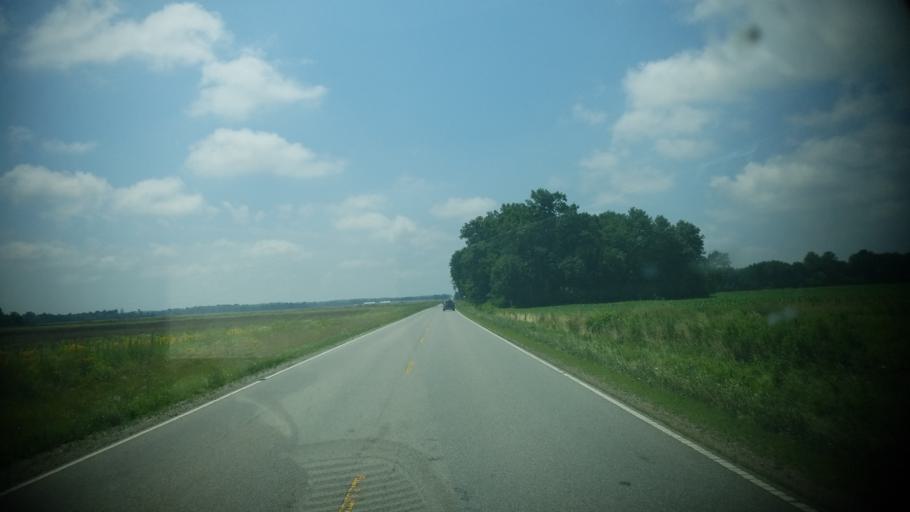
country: US
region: Illinois
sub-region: Wayne County
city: Fairfield
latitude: 38.4649
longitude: -88.3490
